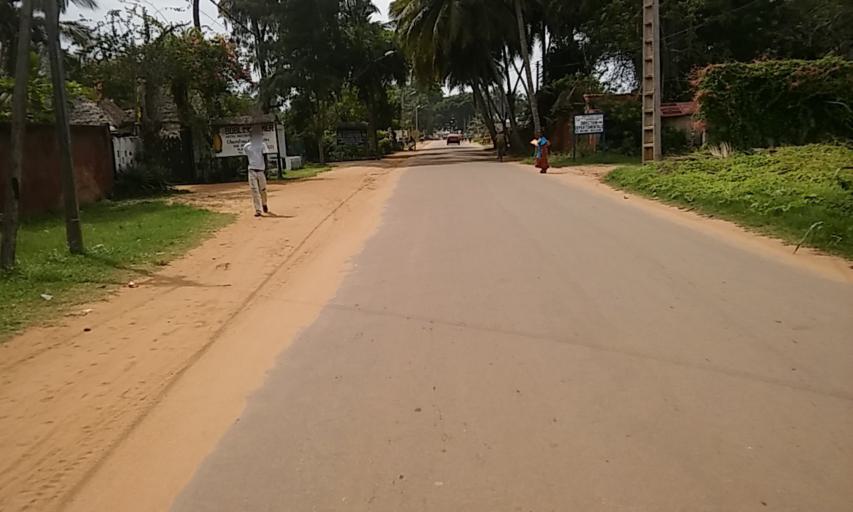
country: CI
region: Sud-Comoe
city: Grand-Bassam
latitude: 5.1966
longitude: -3.7448
